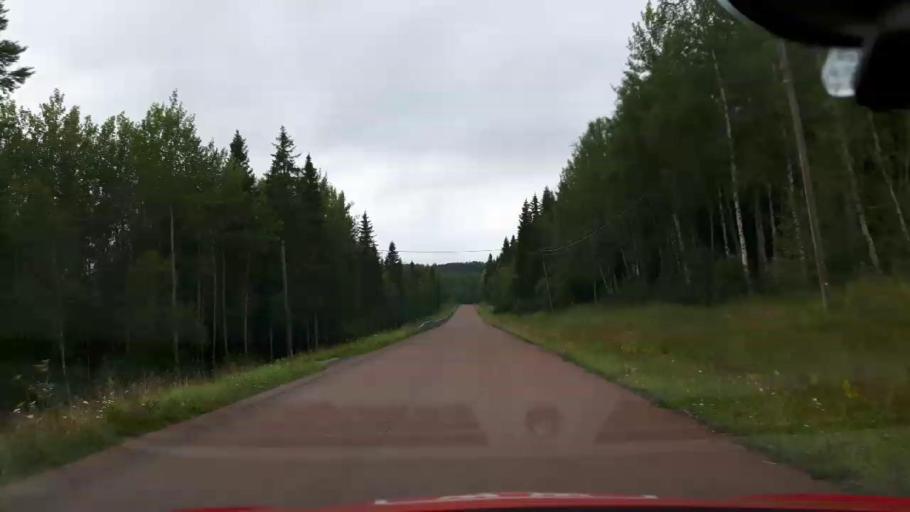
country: SE
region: Jaemtland
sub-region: Krokoms Kommun
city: Valla
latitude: 63.3900
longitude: 13.8934
